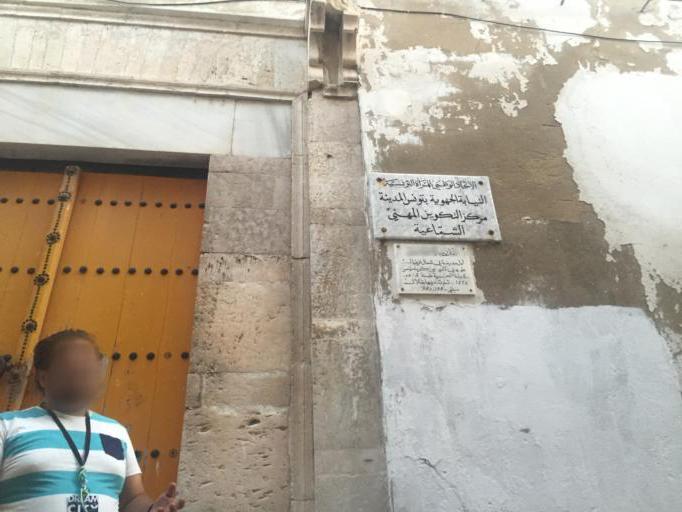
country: TN
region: Tunis
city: Tunis
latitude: 36.7982
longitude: 10.1711
